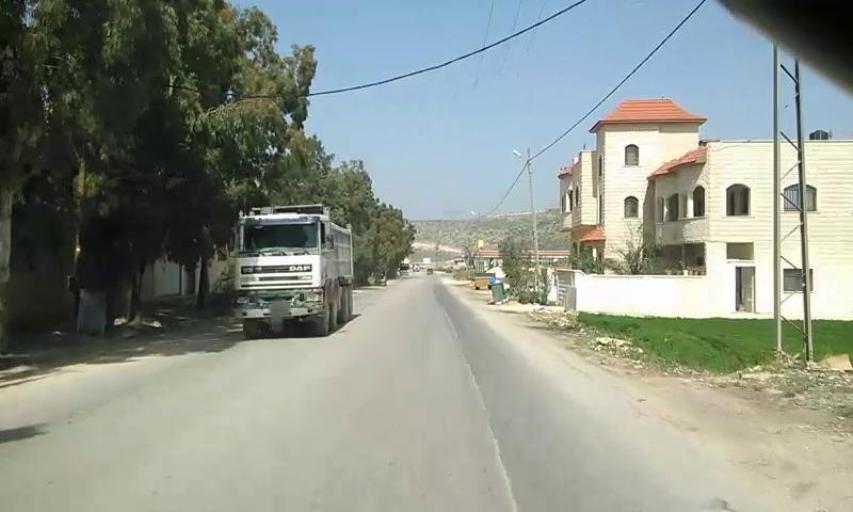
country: PS
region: West Bank
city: Az Zababidah
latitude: 32.3923
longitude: 35.3209
